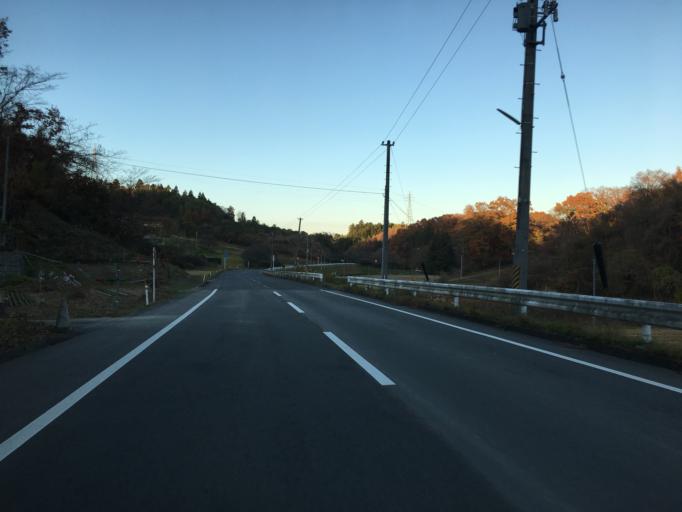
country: JP
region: Fukushima
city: Nihommatsu
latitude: 37.5371
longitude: 140.4587
